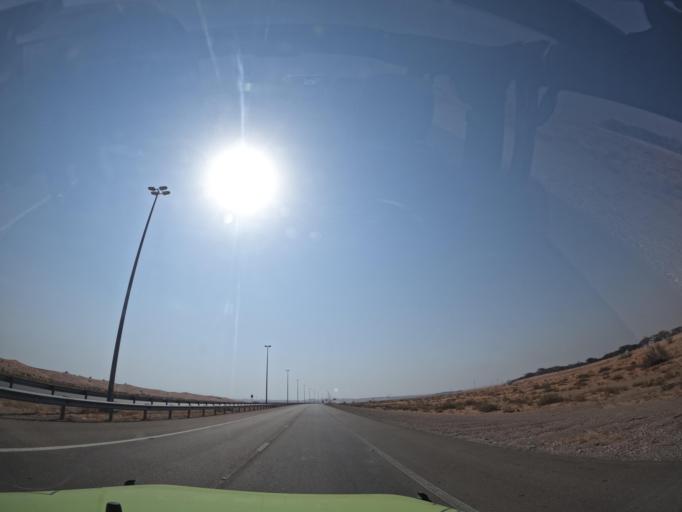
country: OM
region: Al Buraimi
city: Al Buraymi
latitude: 24.3996
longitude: 55.7154
